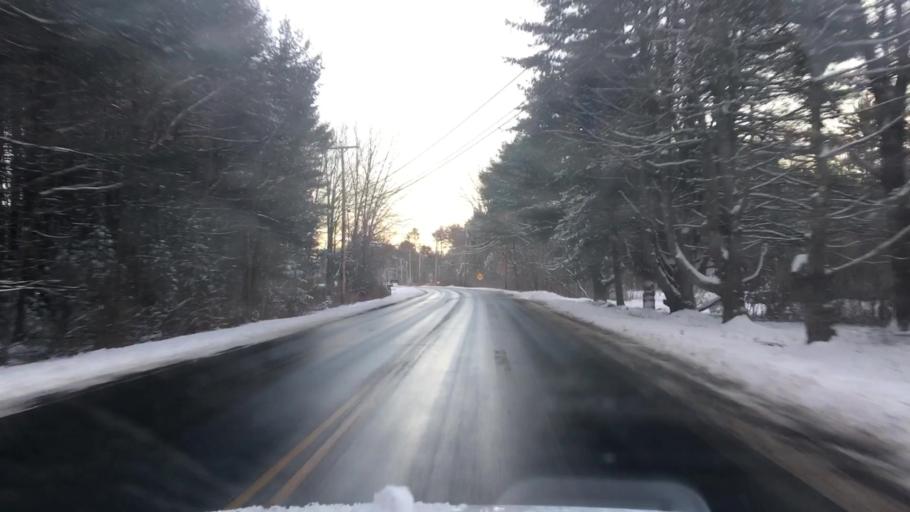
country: US
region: Maine
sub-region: Sagadahoc County
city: Topsham
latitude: 43.9604
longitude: -69.9288
